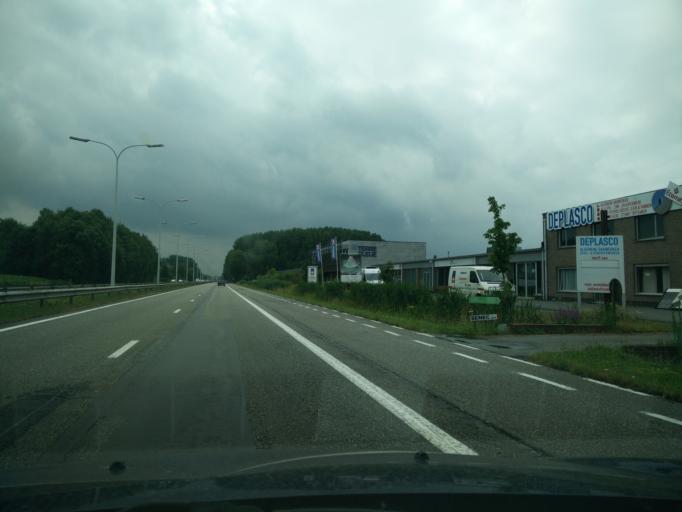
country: BE
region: Flanders
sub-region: Provincie Oost-Vlaanderen
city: De Pinte
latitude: 50.9638
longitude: 3.6515
